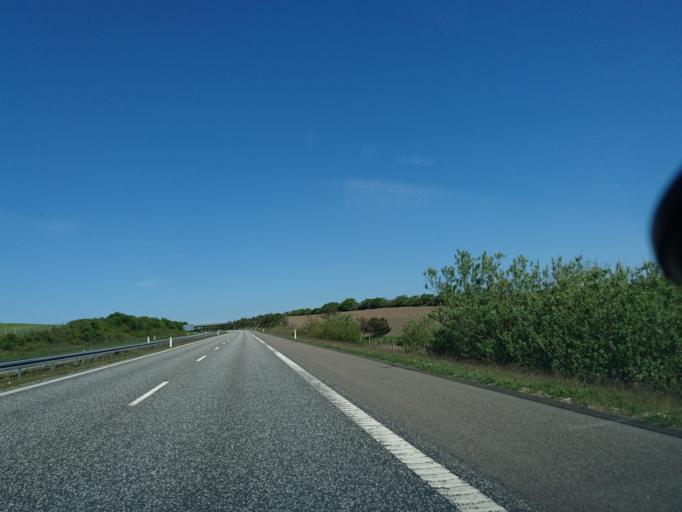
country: DK
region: North Denmark
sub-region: Hjorring Kommune
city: Hjorring
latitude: 57.5224
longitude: 10.0100
